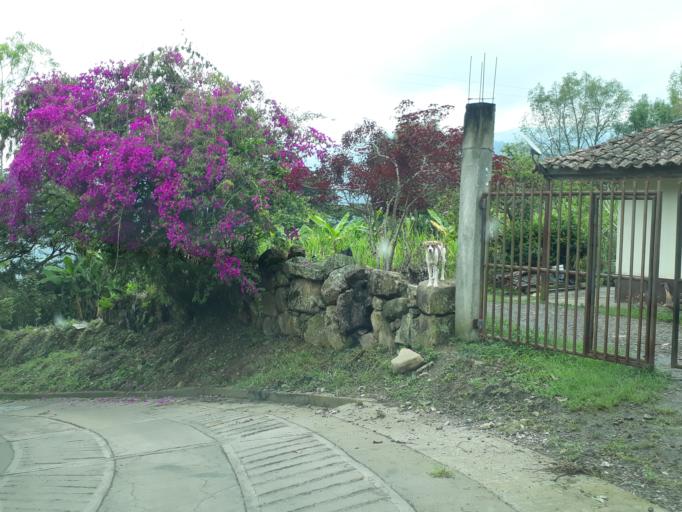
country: CO
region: Cundinamarca
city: Manta
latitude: 4.9926
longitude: -73.5672
